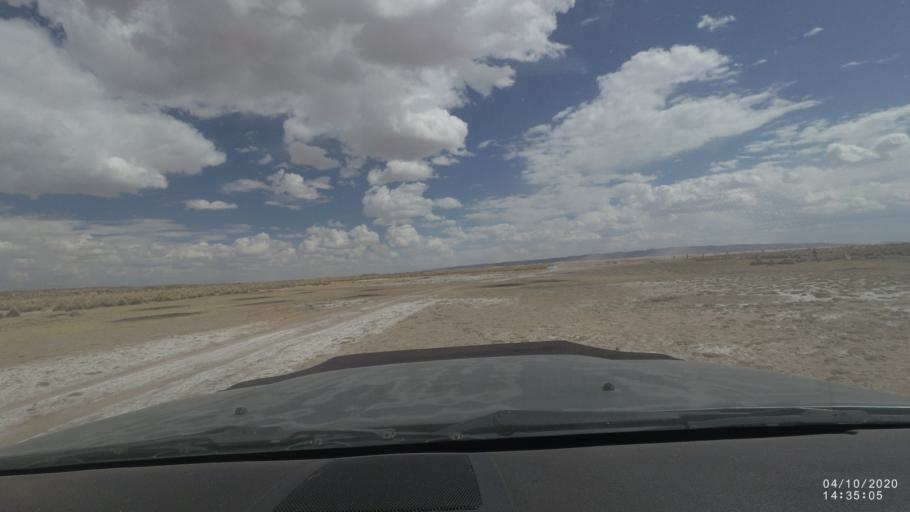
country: BO
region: Oruro
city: Poopo
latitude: -18.6719
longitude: -67.4696
